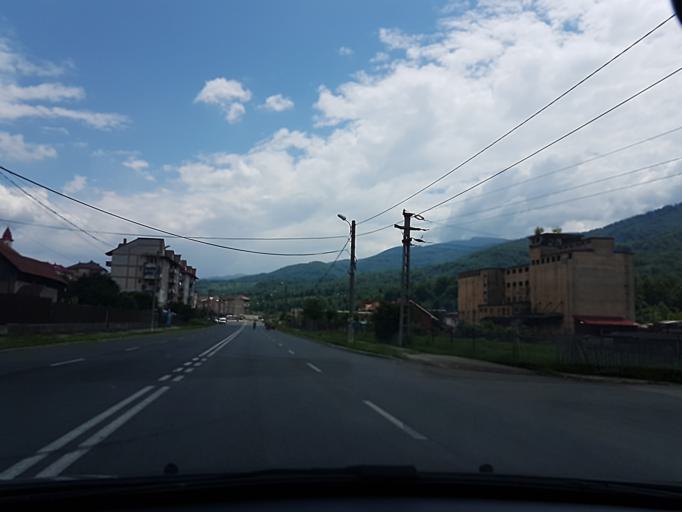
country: RO
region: Hunedoara
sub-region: Comuna Uricani
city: Uricani
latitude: 45.3445
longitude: 23.1814
